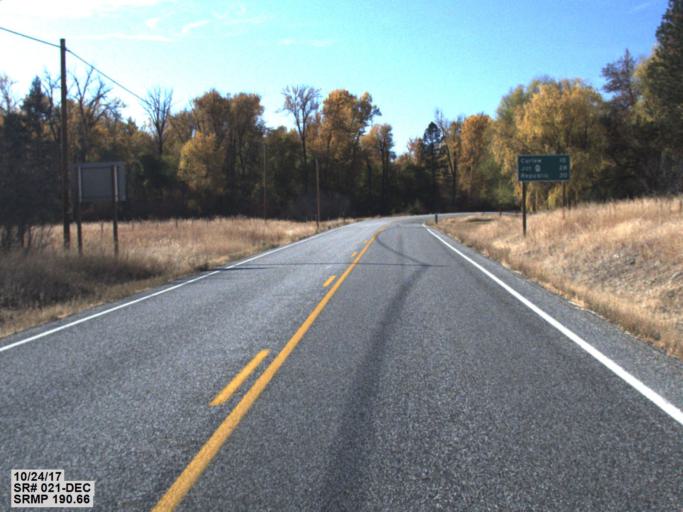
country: CA
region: British Columbia
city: Grand Forks
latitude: 48.9909
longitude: -118.5093
